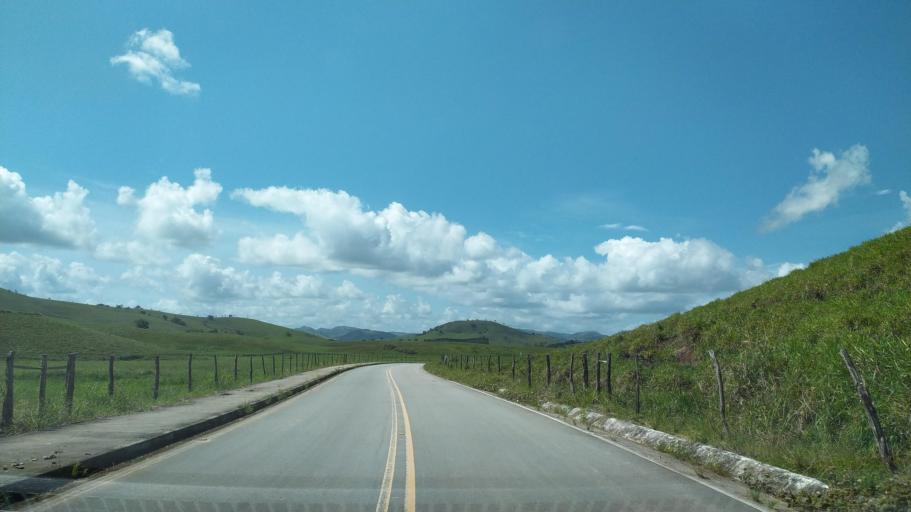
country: BR
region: Alagoas
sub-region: Uniao Dos Palmares
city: Uniao dos Palmares
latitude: -9.1644
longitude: -36.0544
